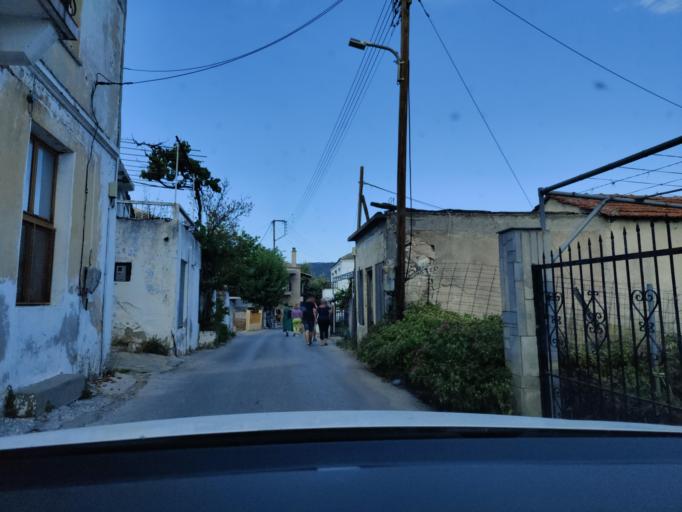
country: GR
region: East Macedonia and Thrace
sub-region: Nomos Kavalas
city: Potamia
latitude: 40.6583
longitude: 24.6904
